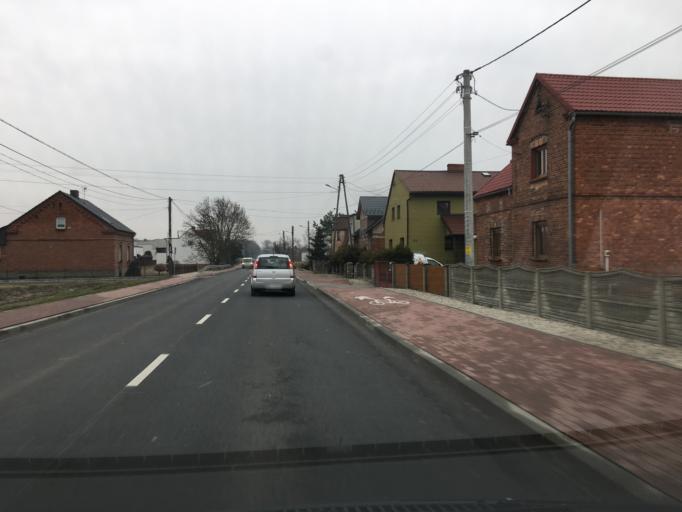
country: PL
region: Opole Voivodeship
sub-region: Powiat kedzierzynsko-kozielski
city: Bierawa
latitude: 50.3101
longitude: 18.2273
